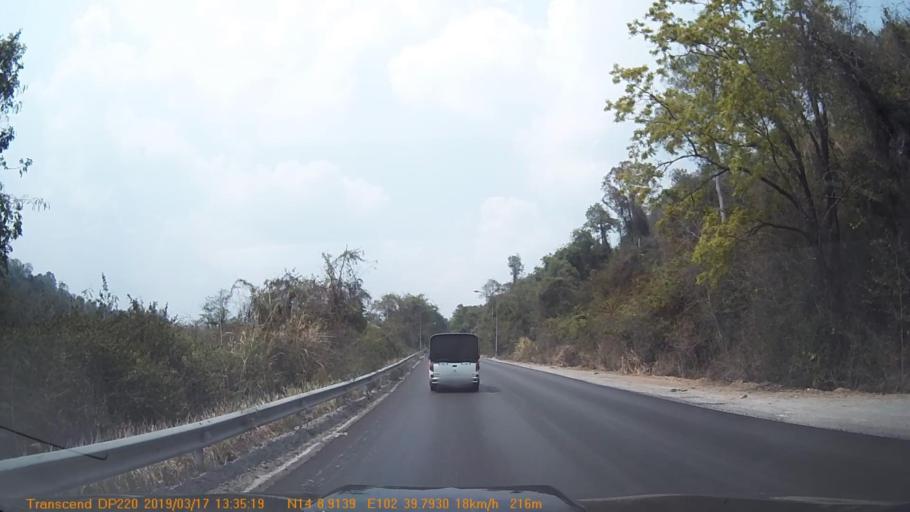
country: TH
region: Buriram
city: Non Din Daeng
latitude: 14.1487
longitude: 102.6632
